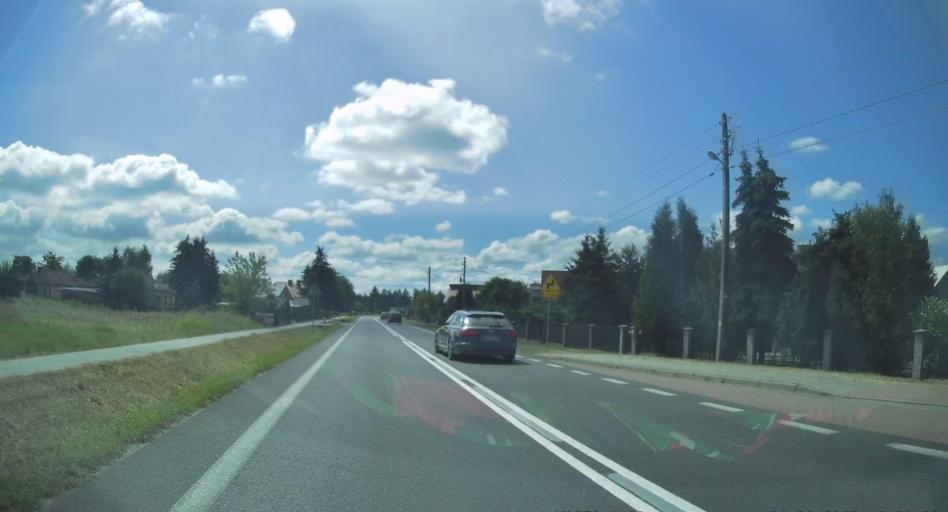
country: PL
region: Subcarpathian Voivodeship
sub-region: Powiat debicki
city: Brzeznica
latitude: 50.1116
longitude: 21.4899
